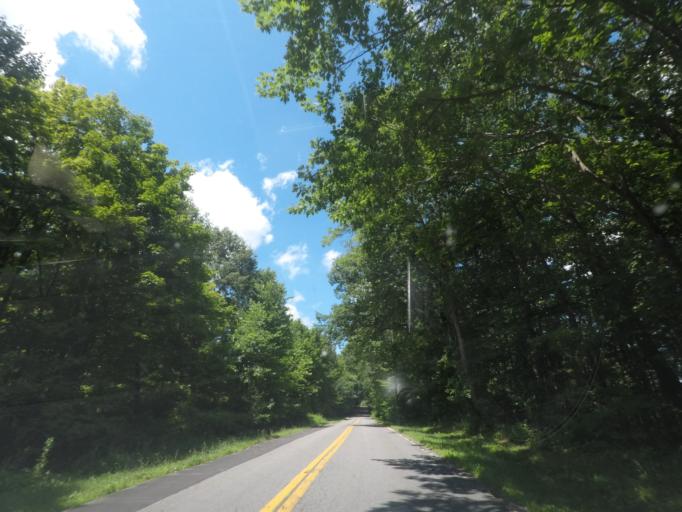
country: US
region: New York
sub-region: Albany County
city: Voorheesville
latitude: 42.7145
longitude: -73.9593
